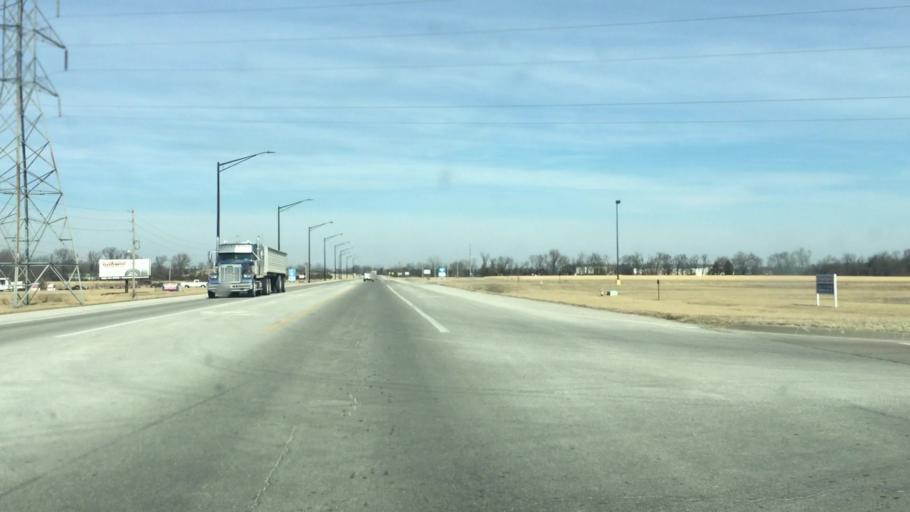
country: US
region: Kansas
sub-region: Labette County
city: Parsons
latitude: 37.3717
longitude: -95.2584
